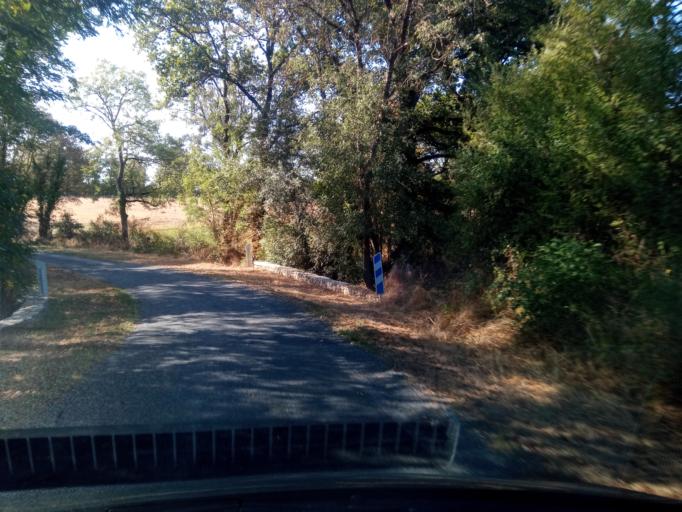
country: FR
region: Poitou-Charentes
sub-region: Departement de la Vienne
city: Saulge
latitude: 46.3705
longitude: 0.8652
